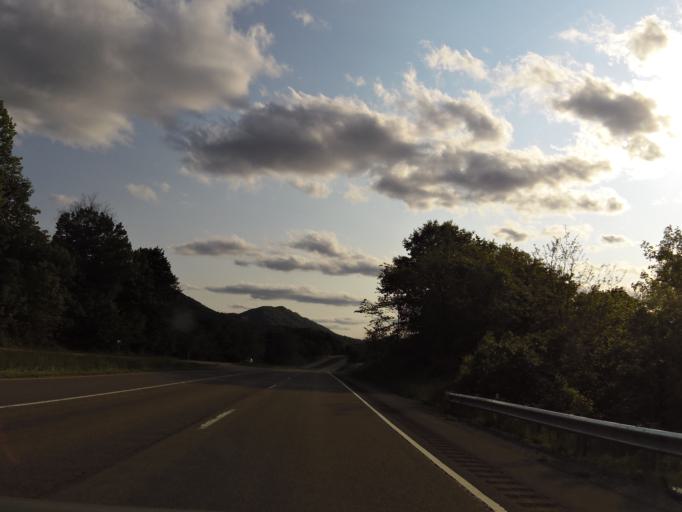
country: US
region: Virginia
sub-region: Tazewell County
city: Tazewell
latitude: 37.1067
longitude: -81.6319
